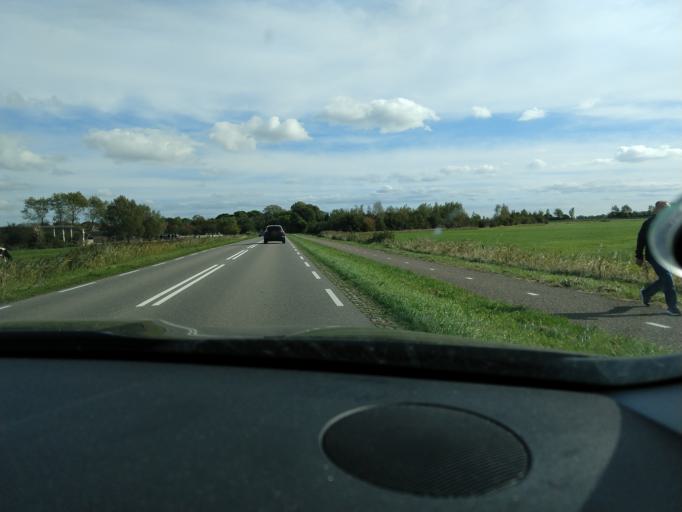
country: NL
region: Zeeland
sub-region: Gemeente Middelburg
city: Middelburg
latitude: 51.5359
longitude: 3.5532
